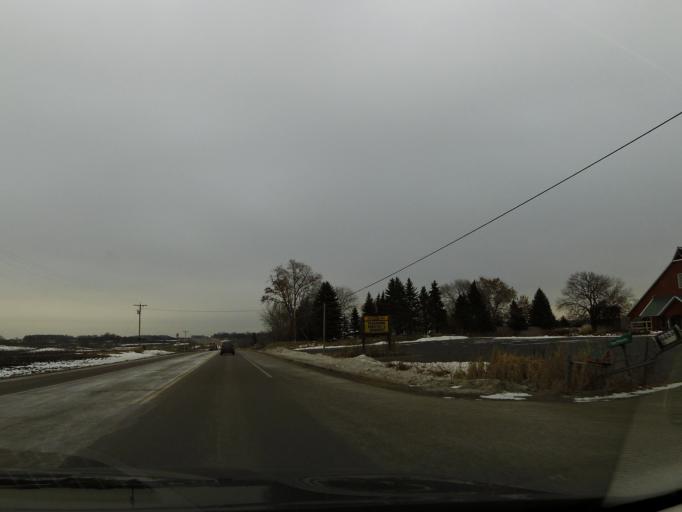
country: US
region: Minnesota
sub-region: Carver County
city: Carver
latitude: 44.7761
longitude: -93.6749
